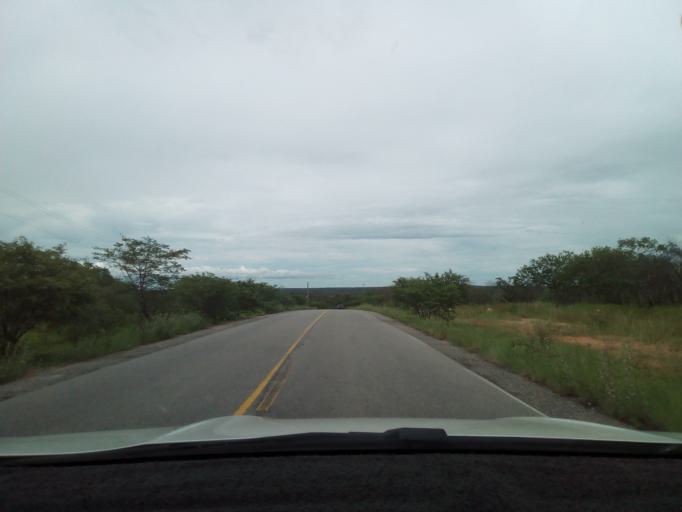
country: BR
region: Rio Grande do Norte
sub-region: Caraubas
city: Caraubas
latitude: -5.8370
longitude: -37.6231
